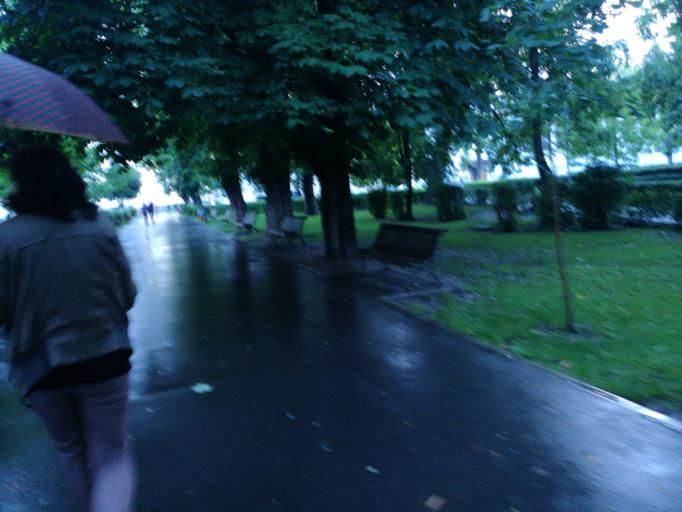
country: RO
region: Brasov
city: Brasov
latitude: 45.6393
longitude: 25.5846
